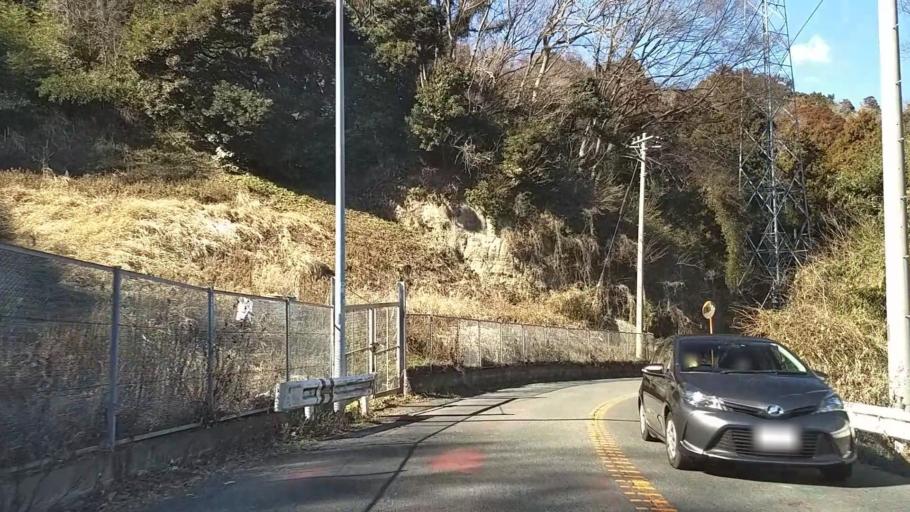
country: JP
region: Kanagawa
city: Zushi
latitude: 35.3310
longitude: 139.5905
